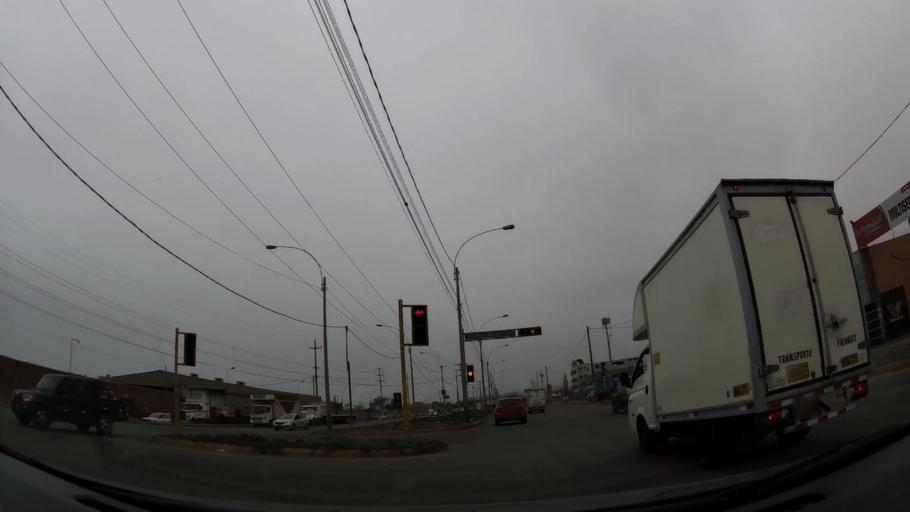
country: PE
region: Callao
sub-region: Callao
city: Callao
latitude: -11.9805
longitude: -77.1251
